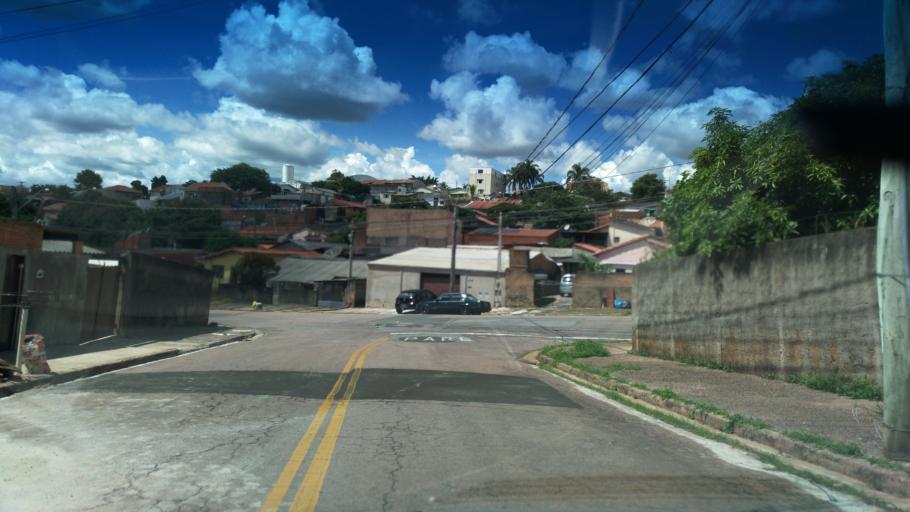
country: BR
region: Sao Paulo
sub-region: Valinhos
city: Valinhos
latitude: -22.9551
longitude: -47.0061
